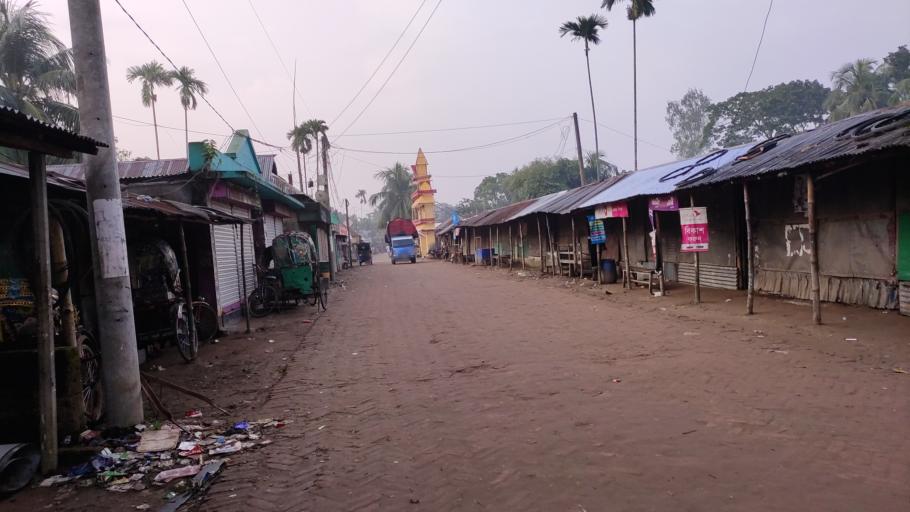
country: BD
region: Dhaka
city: Netrakona
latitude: 24.7156
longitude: 90.9469
